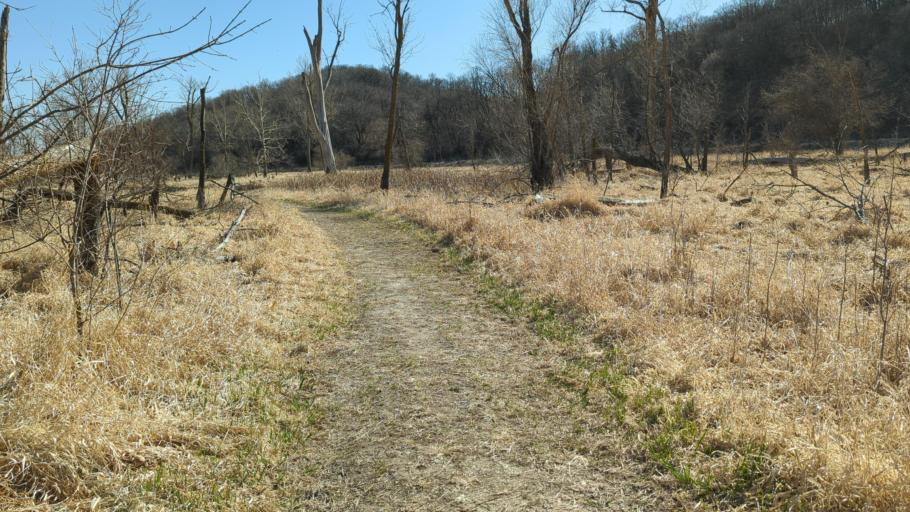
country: US
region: Nebraska
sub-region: Sarpy County
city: Bellevue
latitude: 41.1729
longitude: -95.8905
